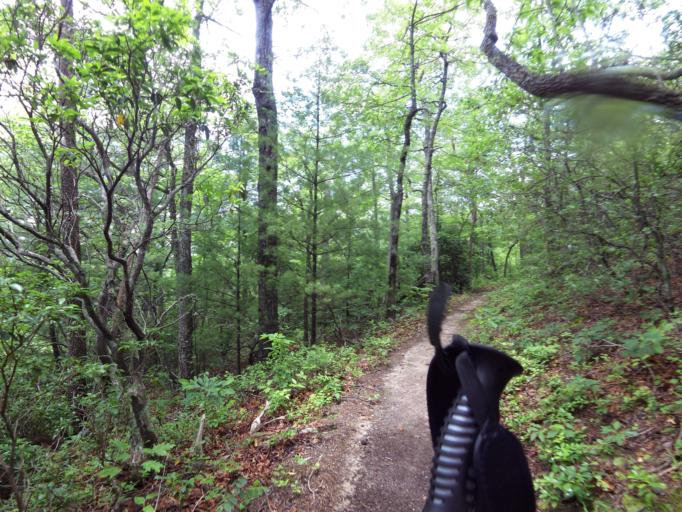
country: US
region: Tennessee
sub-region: Blount County
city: Wildwood
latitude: 35.6577
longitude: -83.8239
